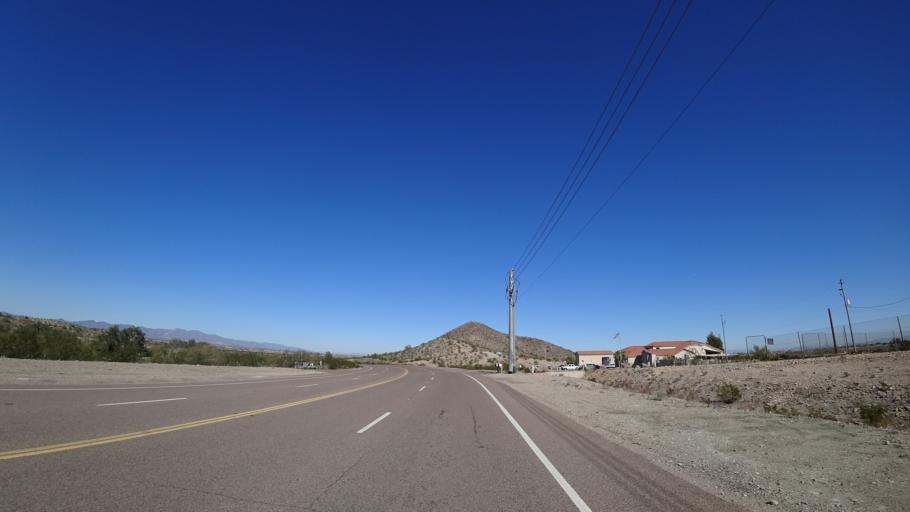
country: US
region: Arizona
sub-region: Maricopa County
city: Goodyear
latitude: 33.3769
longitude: -112.3665
